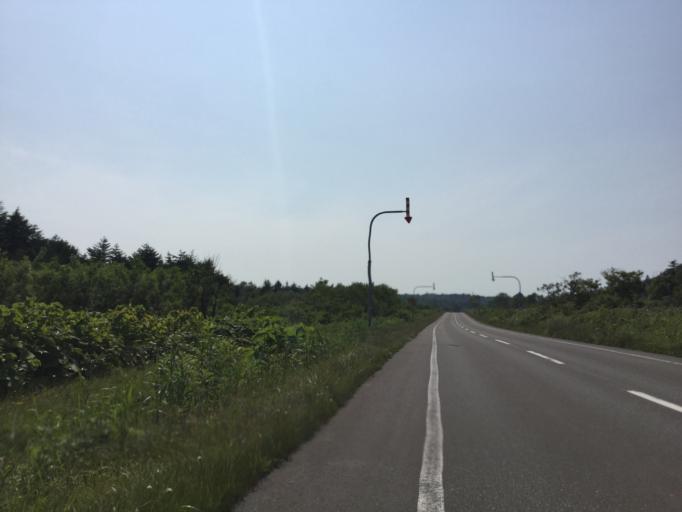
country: JP
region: Hokkaido
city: Makubetsu
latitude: 45.4047
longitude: 142.0369
